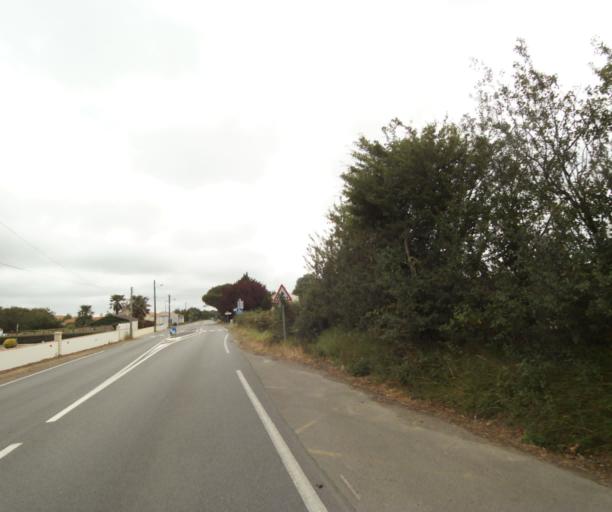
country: FR
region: Pays de la Loire
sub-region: Departement de la Vendee
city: Sainte-Foy
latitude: 46.5143
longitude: -1.6872
